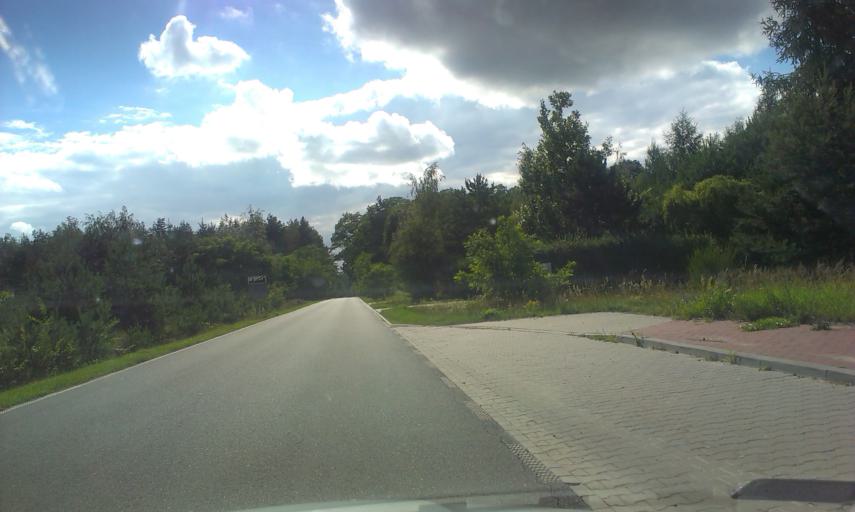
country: PL
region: Masovian Voivodeship
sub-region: Powiat zyrardowski
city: Radziejowice
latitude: 51.9678
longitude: 20.6200
